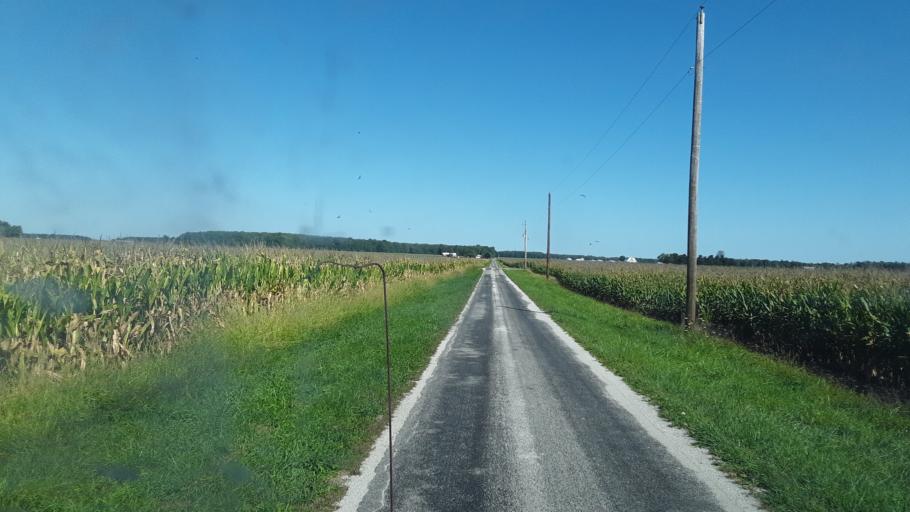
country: US
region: Ohio
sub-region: Crawford County
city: Bucyrus
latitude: 40.9706
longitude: -83.0355
